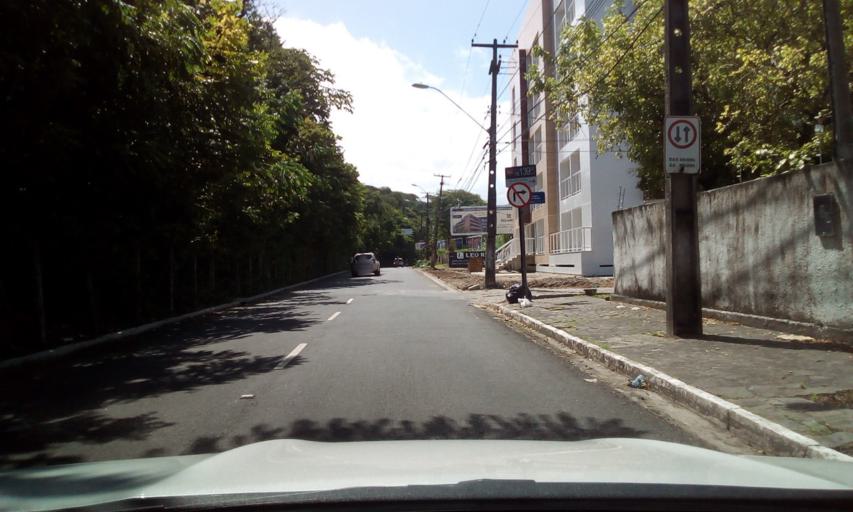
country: BR
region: Paraiba
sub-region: Joao Pessoa
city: Joao Pessoa
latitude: -7.1446
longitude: -34.8135
